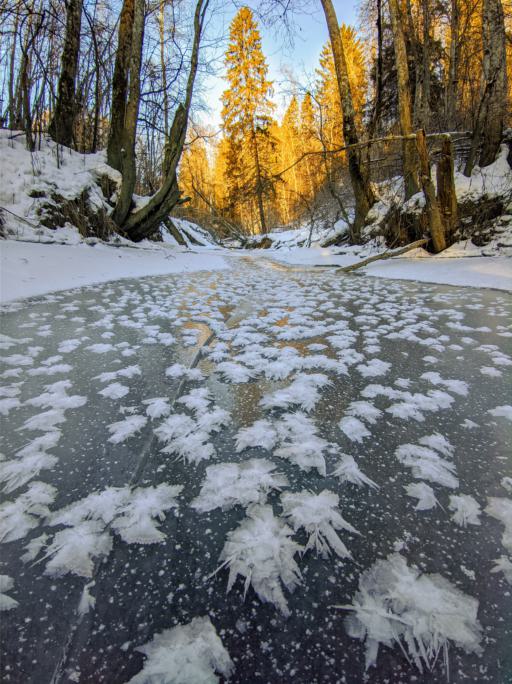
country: NO
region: Akershus
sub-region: Nannestad
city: Teigebyen
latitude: 60.1660
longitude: 11.0593
